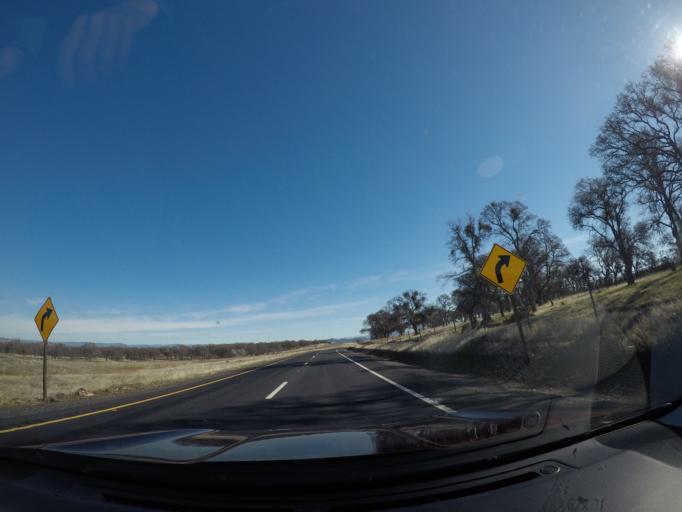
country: US
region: California
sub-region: Calaveras County
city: Copperopolis
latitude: 37.8472
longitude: -120.5730
